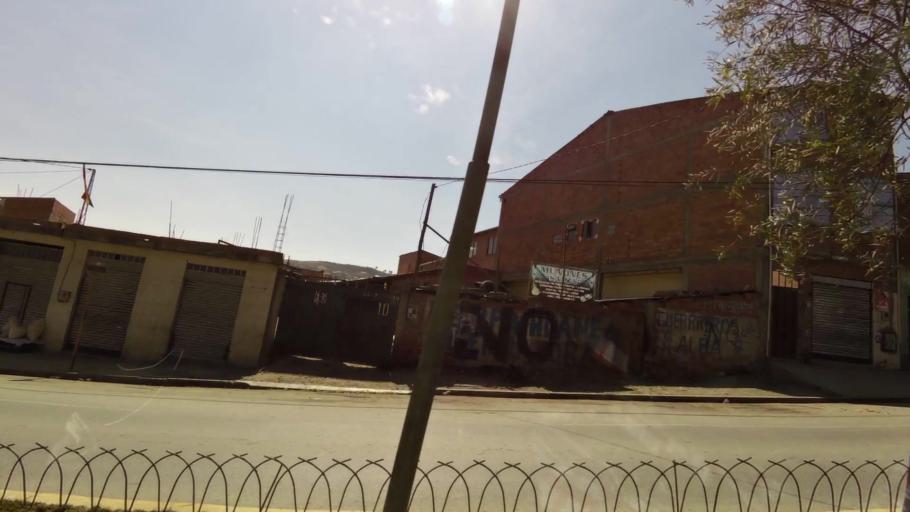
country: BO
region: La Paz
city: La Paz
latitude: -16.5342
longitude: -68.0396
